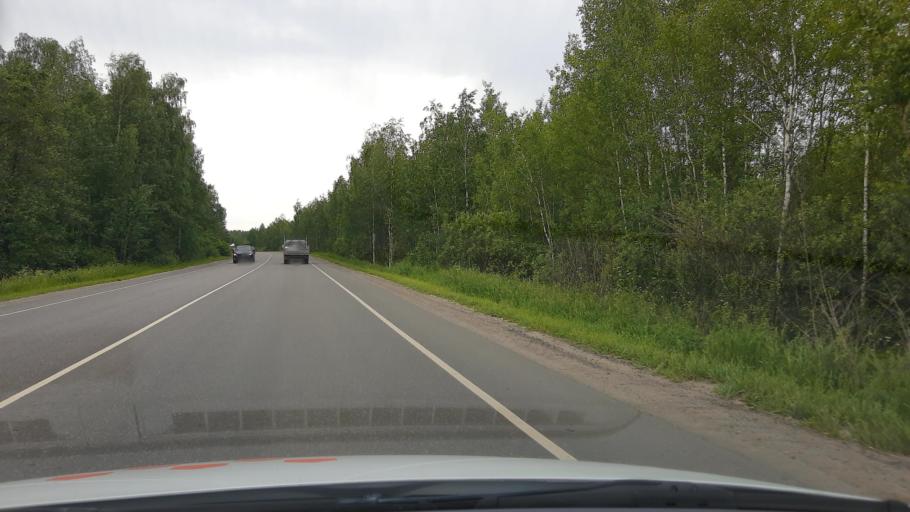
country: RU
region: Moskovskaya
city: Noginsk
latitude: 55.8661
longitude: 38.4178
